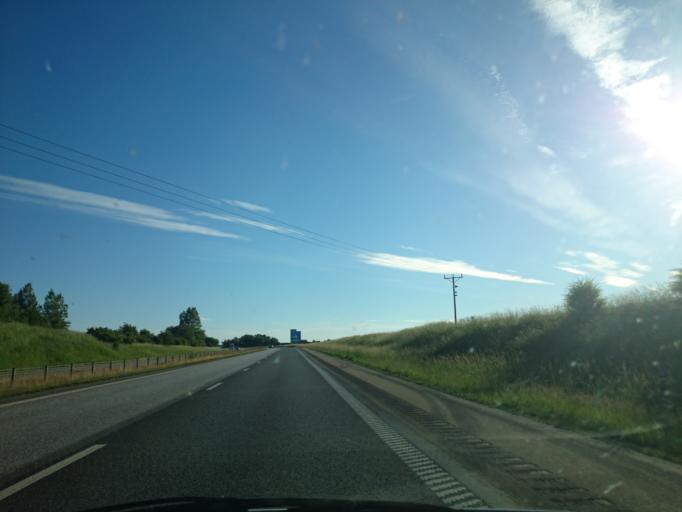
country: SE
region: Skane
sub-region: Helsingborg
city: Hyllinge
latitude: 56.1118
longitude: 12.8712
